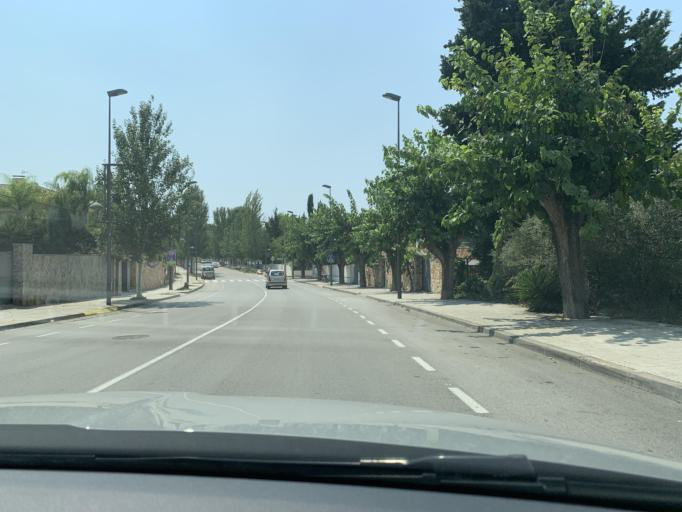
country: ES
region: Catalonia
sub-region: Provincia de Tarragona
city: Altafulla
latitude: 41.1348
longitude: 1.3460
